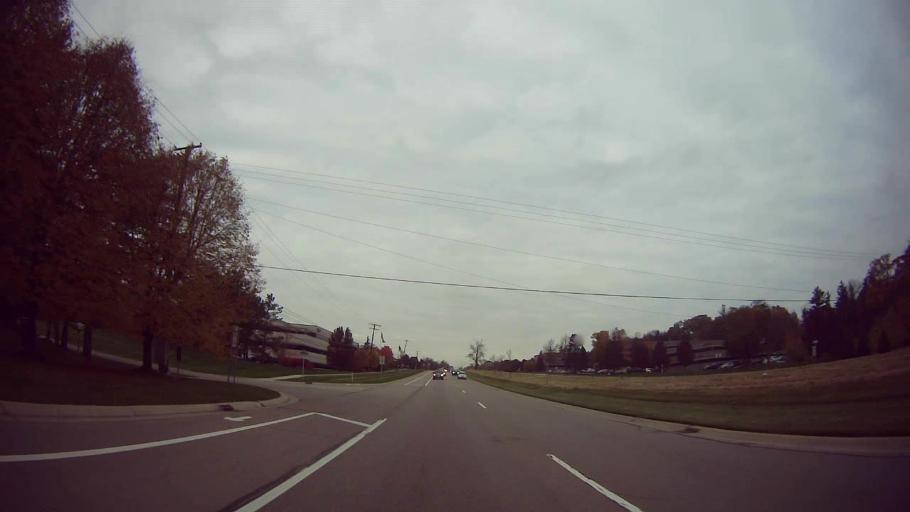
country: US
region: Michigan
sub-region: Oakland County
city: Franklin
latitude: 42.5100
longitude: -83.3254
